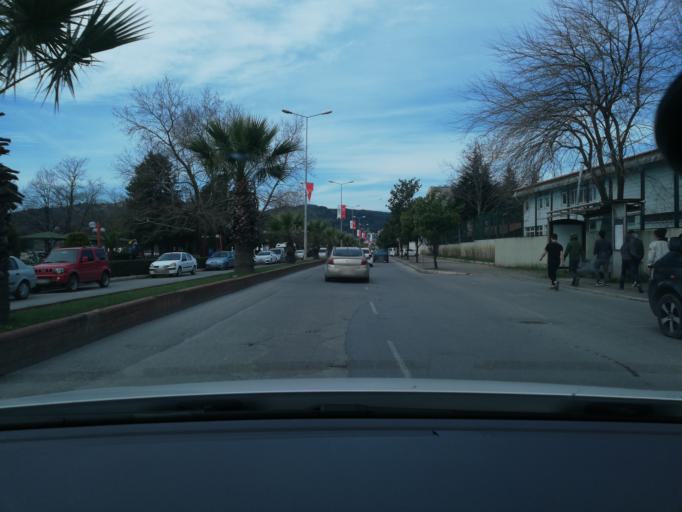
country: TR
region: Zonguldak
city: Eregli
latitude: 41.2851
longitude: 31.4127
